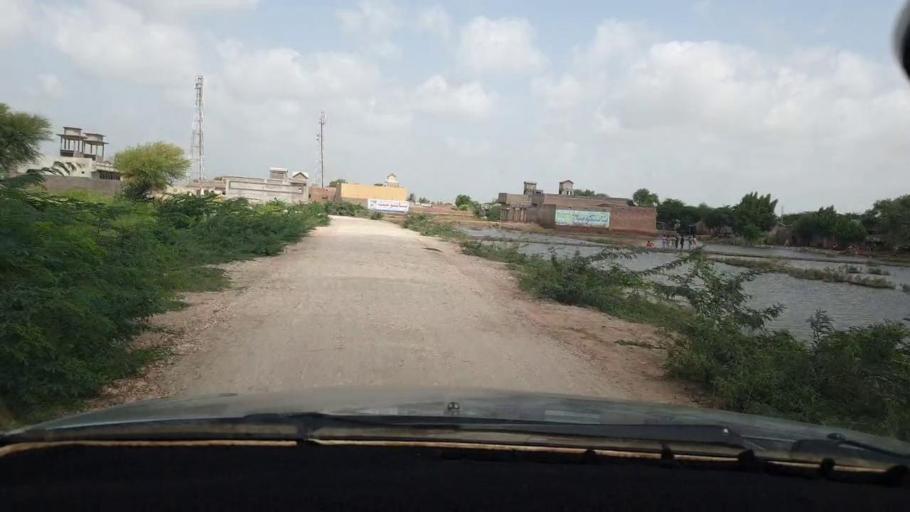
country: PK
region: Sindh
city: Tando Bago
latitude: 24.7597
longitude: 69.1917
